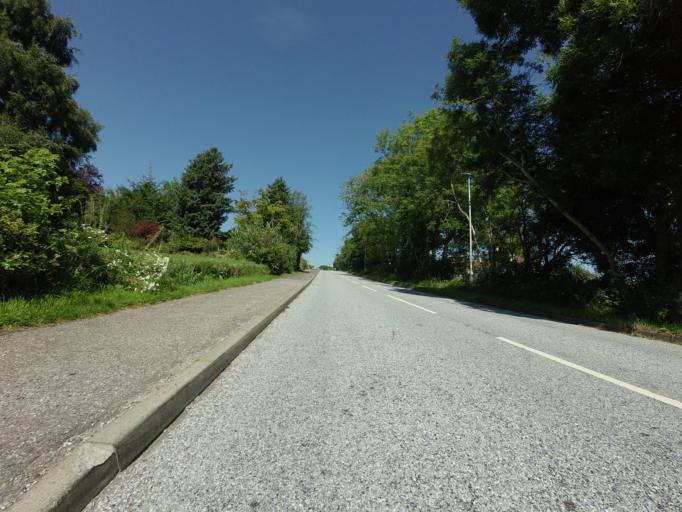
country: GB
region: Scotland
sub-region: Highland
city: Dingwall
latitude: 57.6080
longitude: -4.4216
